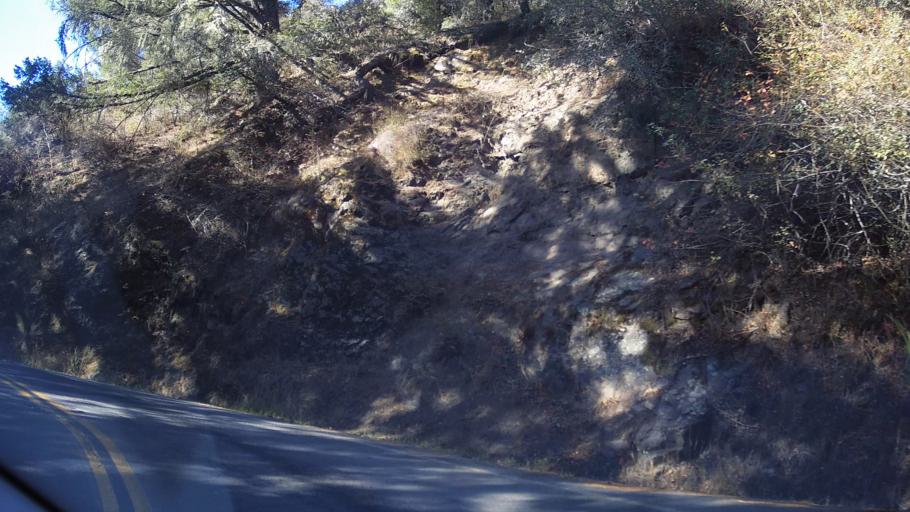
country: US
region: California
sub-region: Marin County
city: Mill Valley
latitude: 37.9108
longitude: -122.5941
